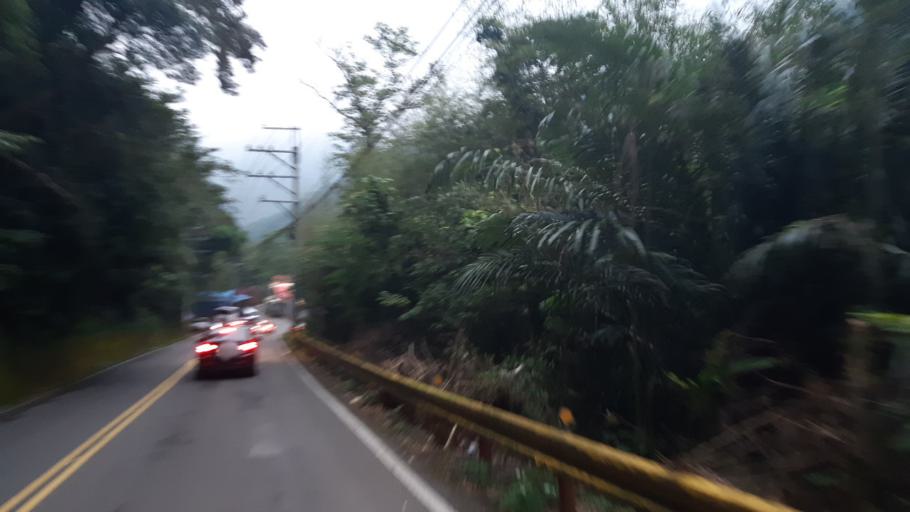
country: TW
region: Taiwan
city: Daxi
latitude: 24.7010
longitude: 121.2147
